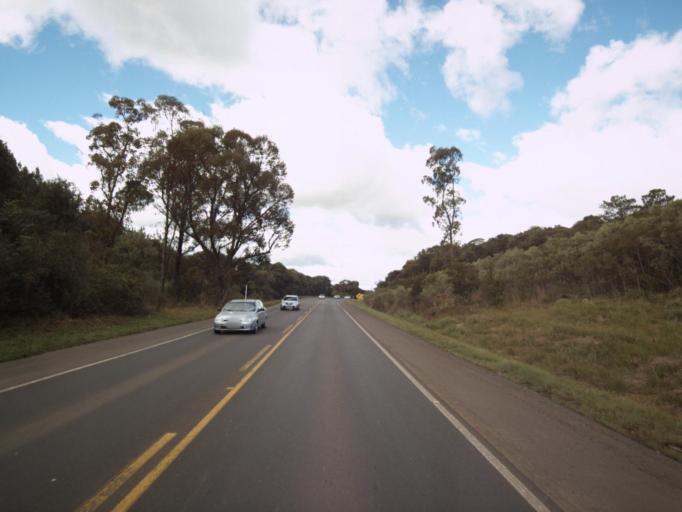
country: BR
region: Santa Catarina
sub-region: Joacaba
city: Joacaba
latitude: -27.0399
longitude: -51.7093
